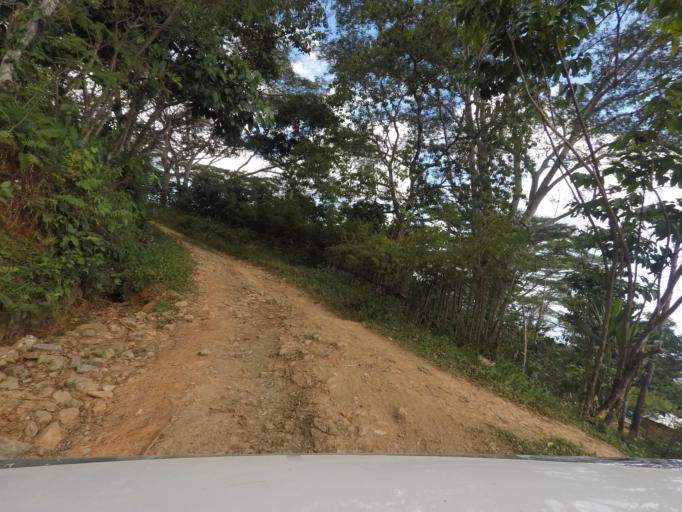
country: TL
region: Ermera
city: Gleno
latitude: -8.7191
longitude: 125.3182
